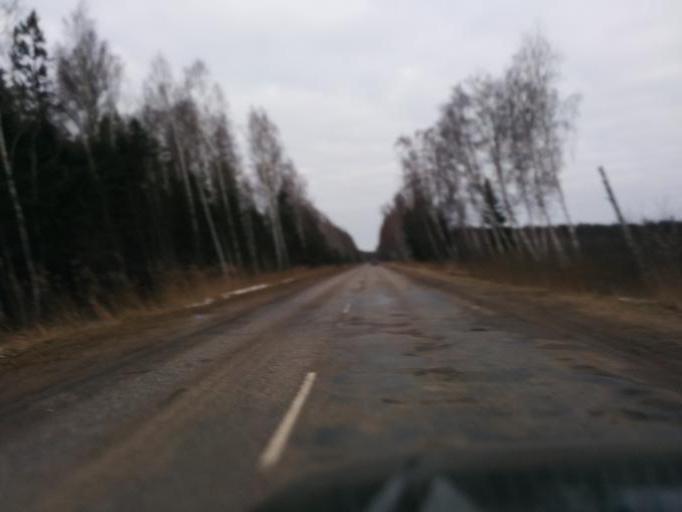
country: LV
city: Tireli
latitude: 56.9069
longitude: 23.5281
